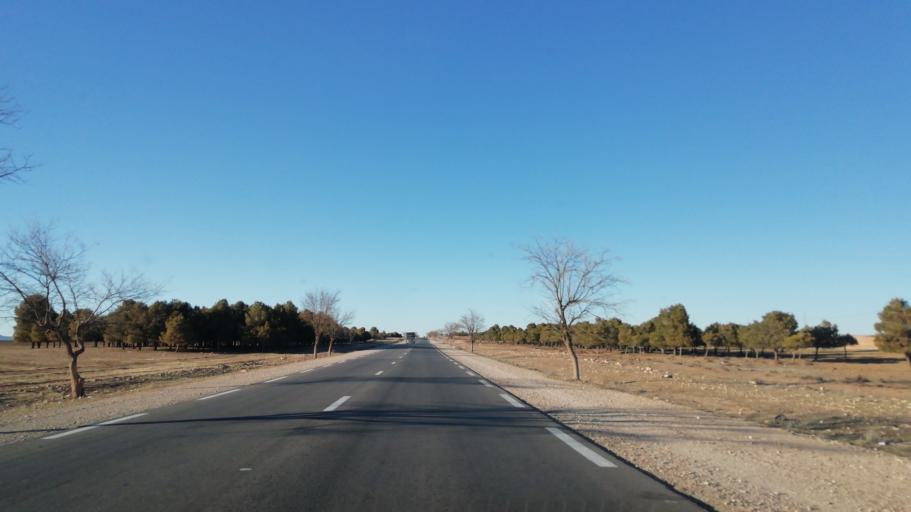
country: DZ
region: Tlemcen
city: Sebdou
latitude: 34.5243
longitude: -1.2912
